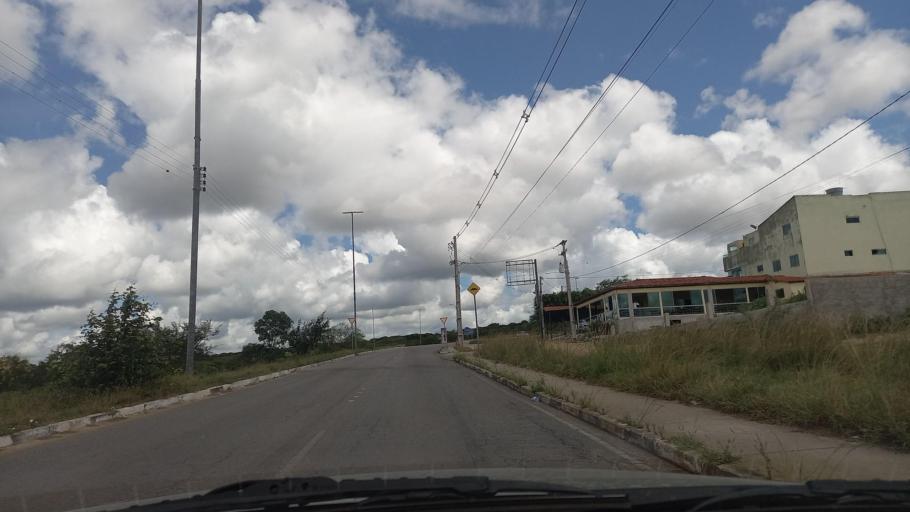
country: BR
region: Pernambuco
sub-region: Caruaru
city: Caruaru
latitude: -8.2924
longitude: -35.9412
